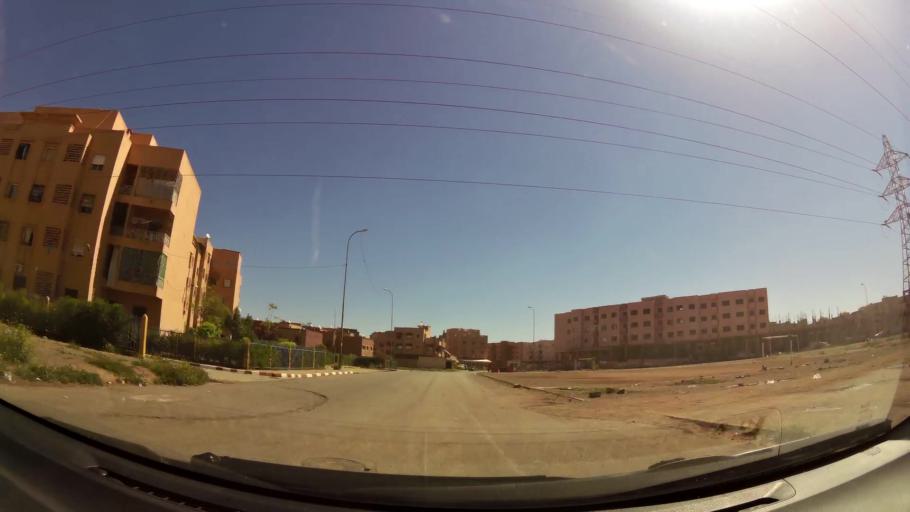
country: MA
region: Marrakech-Tensift-Al Haouz
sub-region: Marrakech
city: Marrakesh
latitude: 31.5743
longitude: -8.0618
